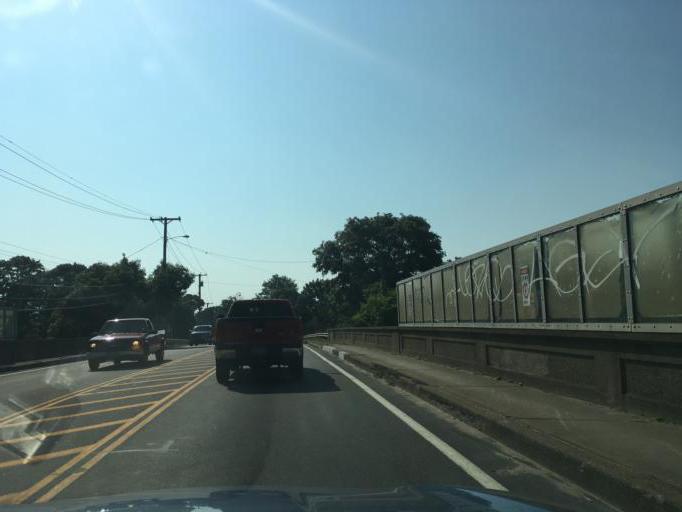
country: US
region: Rhode Island
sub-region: Washington County
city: Kingston
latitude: 41.4847
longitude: -71.5601
